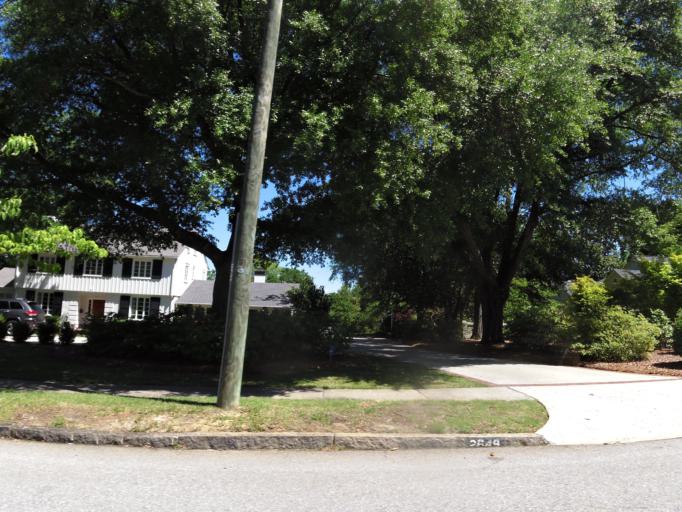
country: US
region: Georgia
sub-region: Richmond County
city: Augusta
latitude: 33.4807
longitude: -82.0300
